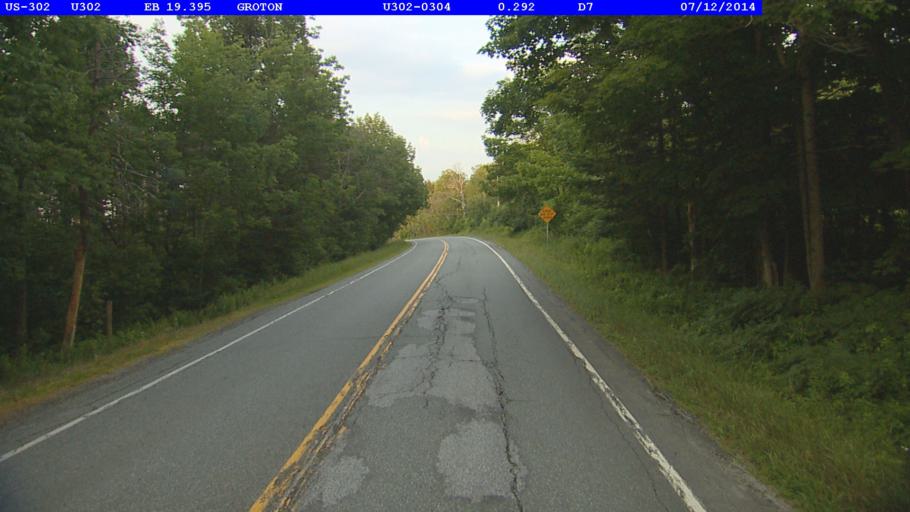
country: US
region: Vermont
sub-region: Washington County
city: Barre
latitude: 44.1869
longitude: -72.2945
